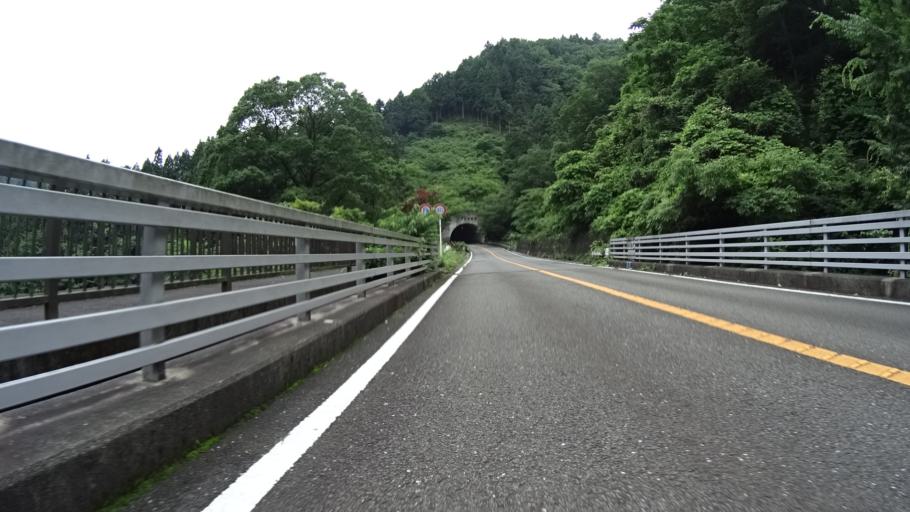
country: JP
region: Kanagawa
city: Hadano
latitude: 35.5139
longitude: 139.2322
